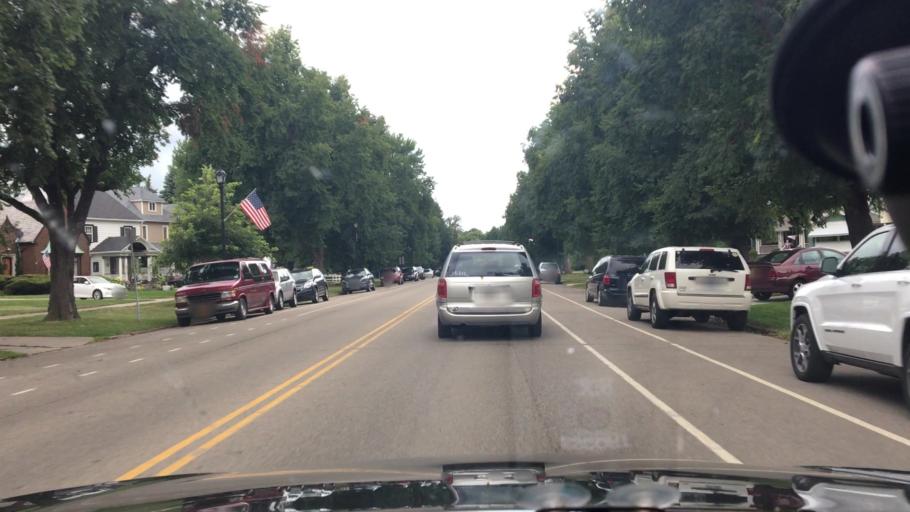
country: US
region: New York
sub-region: Erie County
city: West Seneca
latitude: 42.8531
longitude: -78.8216
